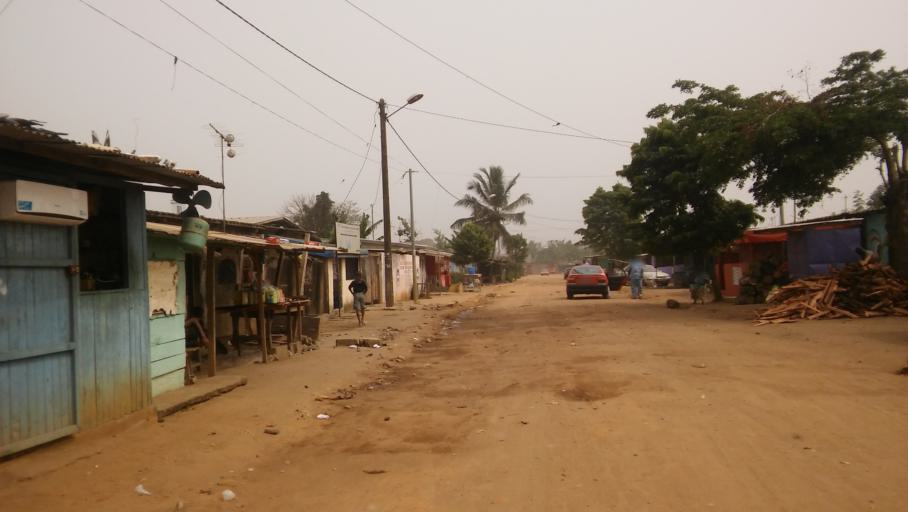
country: CI
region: Sud-Comoe
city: Grand-Bassam
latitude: 5.2146
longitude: -3.7360
